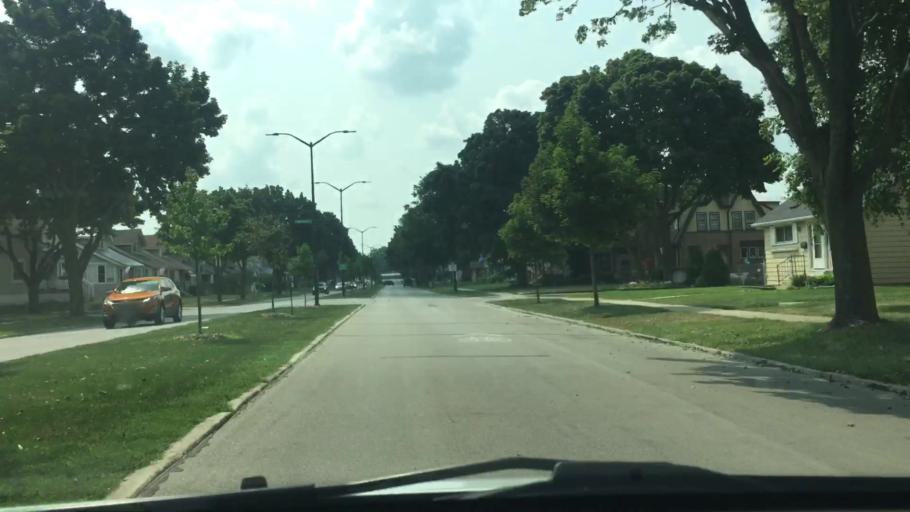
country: US
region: Wisconsin
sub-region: Milwaukee County
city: West Allis
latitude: 43.0209
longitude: -88.0073
